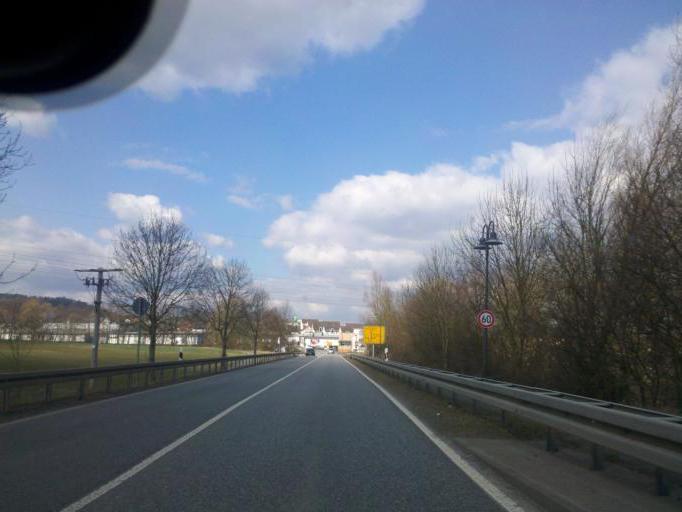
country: DE
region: Hesse
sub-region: Regierungsbezirk Giessen
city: Biedenkopf
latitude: 50.8513
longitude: 8.5474
